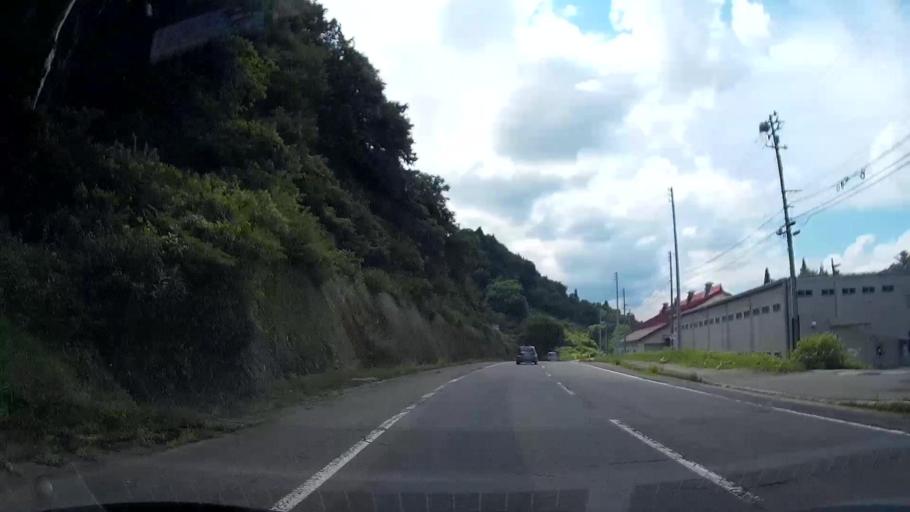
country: JP
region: Niigata
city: Tokamachi
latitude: 37.0011
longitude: 138.6269
